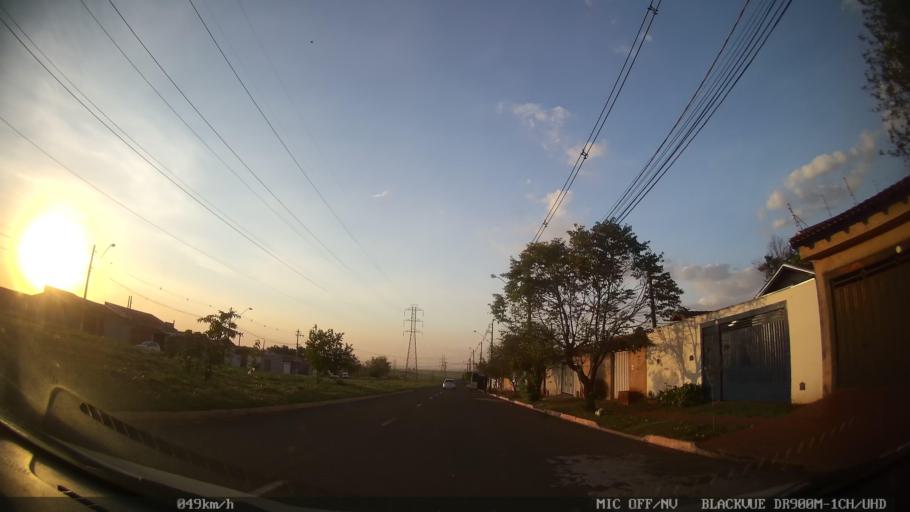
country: BR
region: Sao Paulo
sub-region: Ribeirao Preto
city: Ribeirao Preto
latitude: -21.1396
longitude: -47.8573
